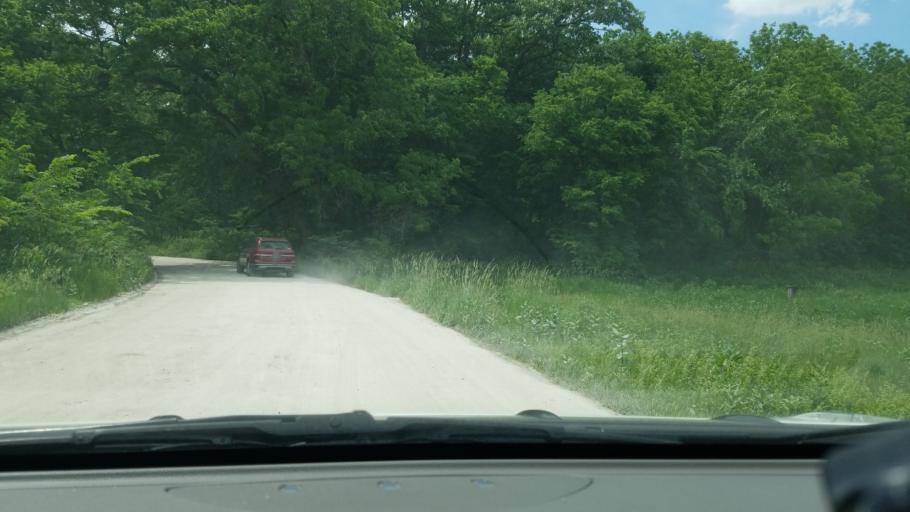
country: US
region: Nebraska
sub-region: Saunders County
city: Ashland
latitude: 41.0108
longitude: -96.2940
